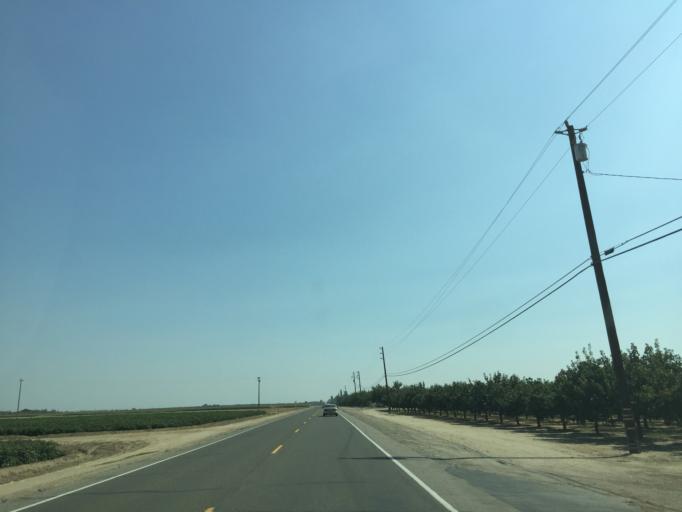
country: US
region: California
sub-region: Kings County
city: Lucerne
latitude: 36.3952
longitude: -119.6730
